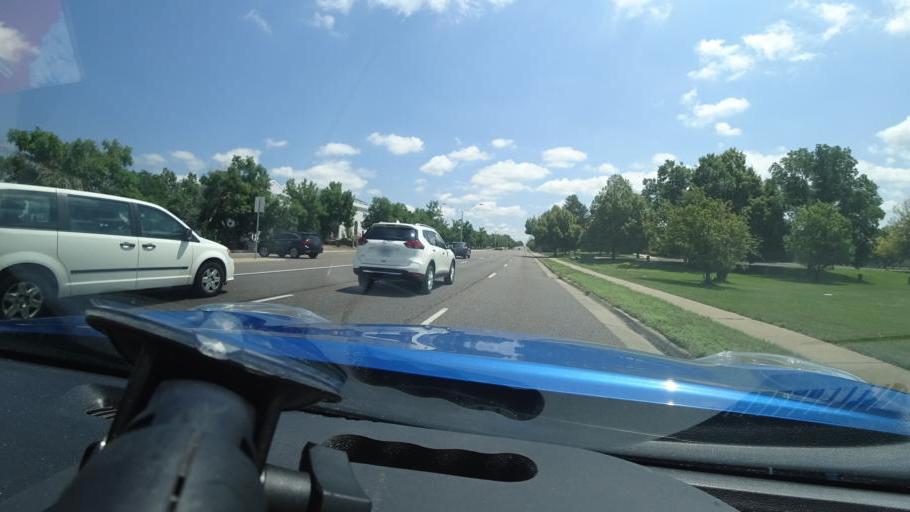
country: US
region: Colorado
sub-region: Adams County
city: Aurora
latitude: 39.7110
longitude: -104.8598
